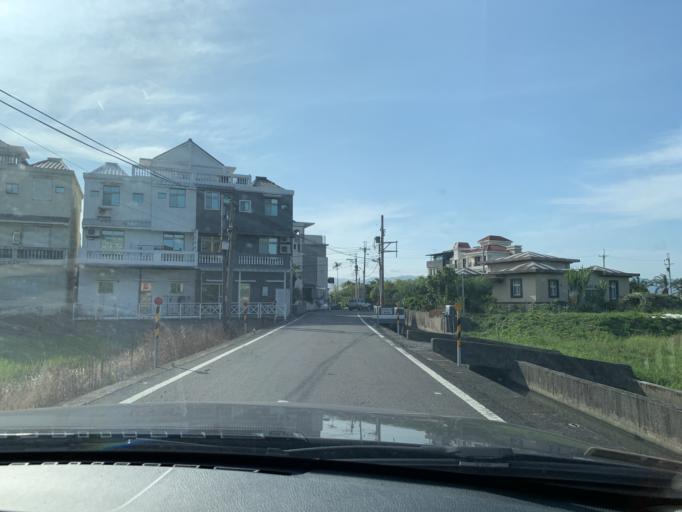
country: TW
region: Taiwan
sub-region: Yilan
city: Yilan
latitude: 24.6784
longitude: 121.8089
